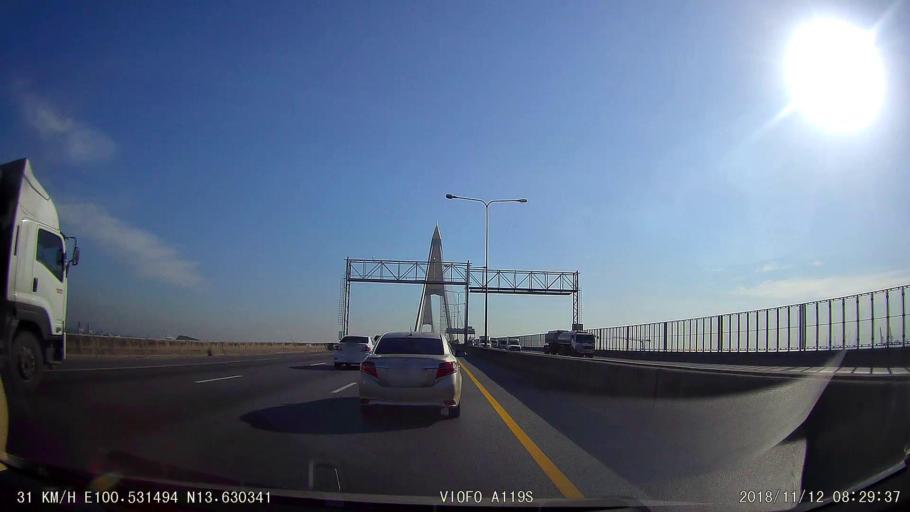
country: TH
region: Bangkok
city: Thung Khru
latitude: 13.6303
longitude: 100.5315
